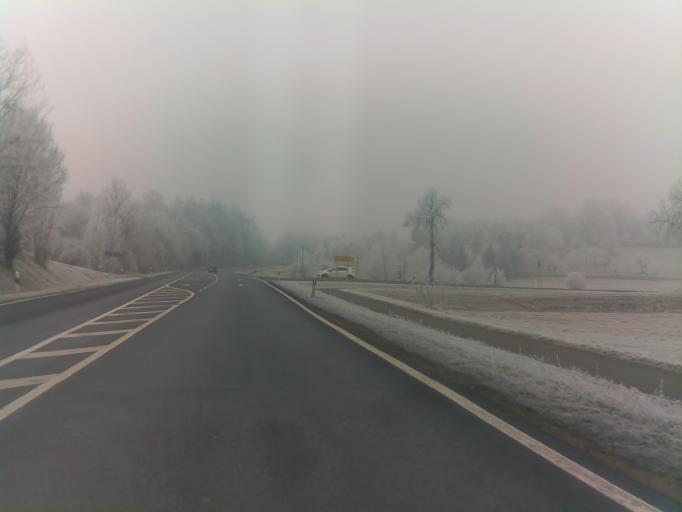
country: DE
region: Bavaria
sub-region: Regierungsbezirk Unterfranken
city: Hassfurt
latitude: 50.0555
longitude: 10.5251
